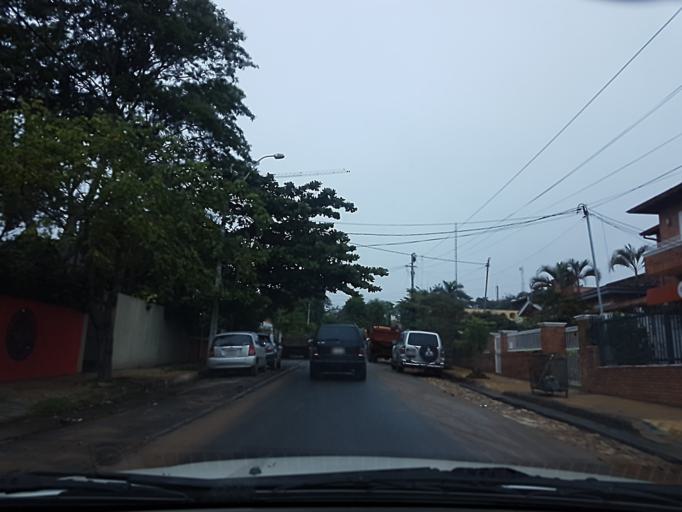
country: PY
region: Asuncion
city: Asuncion
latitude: -25.2843
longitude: -57.6124
